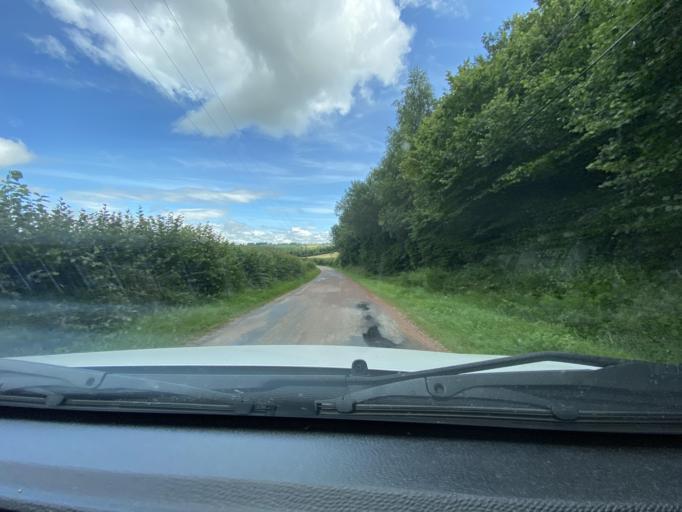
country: FR
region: Bourgogne
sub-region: Departement de la Cote-d'Or
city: Saulieu
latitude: 47.2636
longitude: 4.1939
